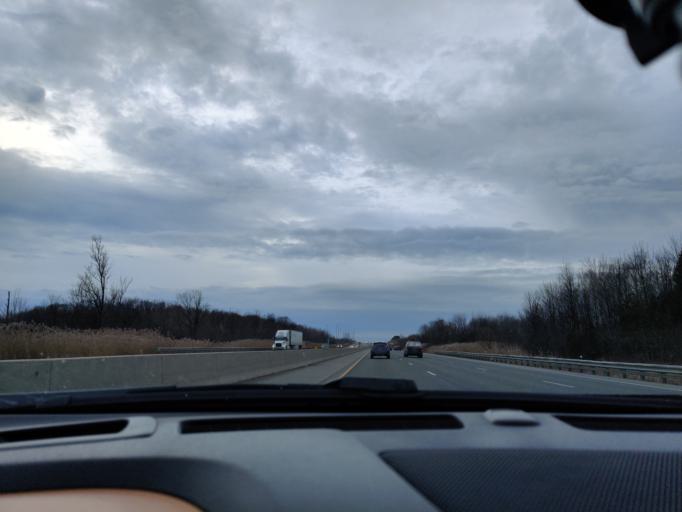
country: CA
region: Ontario
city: Cobourg
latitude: 43.9471
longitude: -78.4176
